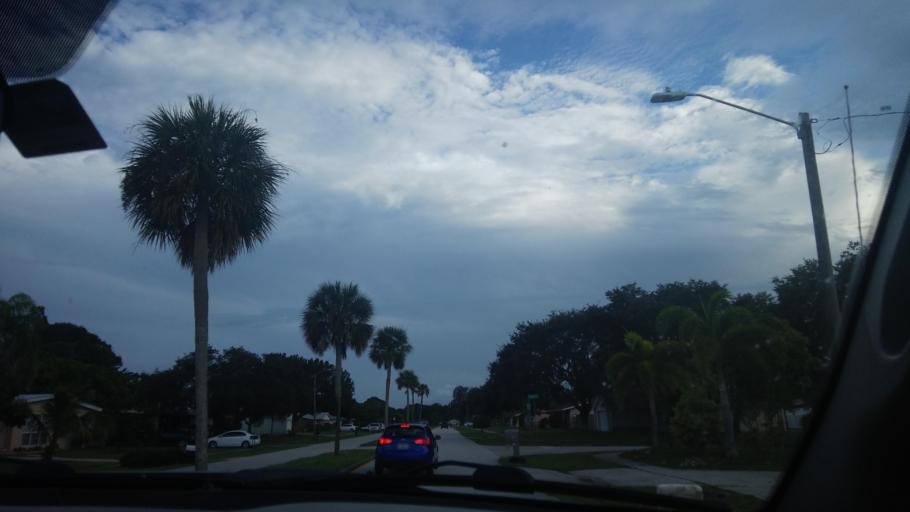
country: US
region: Florida
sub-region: Indian River County
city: Sebastian
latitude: 27.7855
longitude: -80.4628
